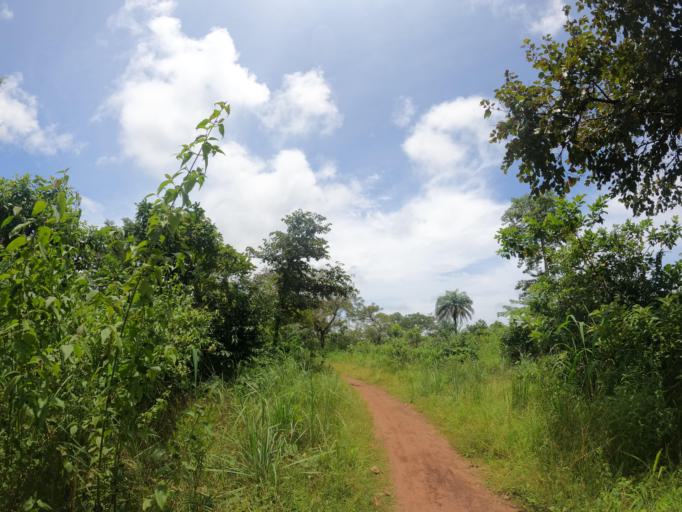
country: SL
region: Northern Province
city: Binkolo
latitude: 9.1472
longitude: -12.2455
